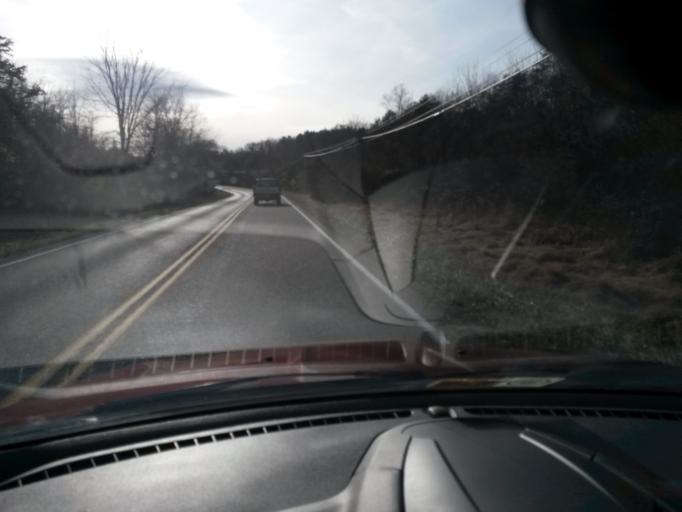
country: US
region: Virginia
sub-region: Rockbridge County
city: East Lexington
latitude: 38.0699
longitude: -79.4016
